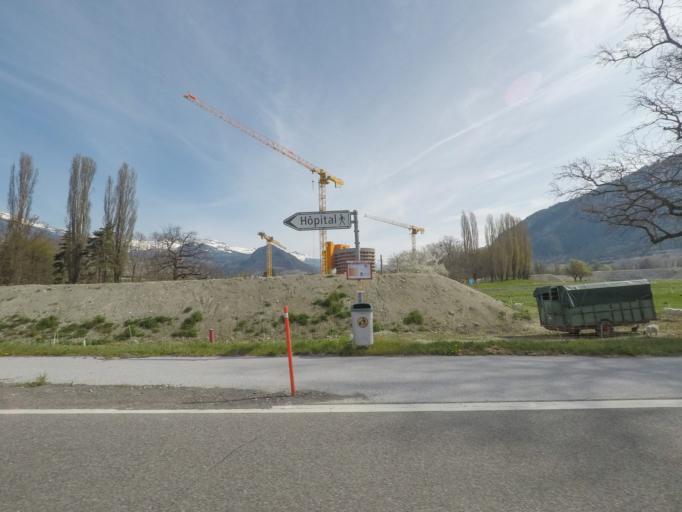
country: CH
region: Valais
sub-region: Sion District
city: Sitten
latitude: 46.2330
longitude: 7.3838
